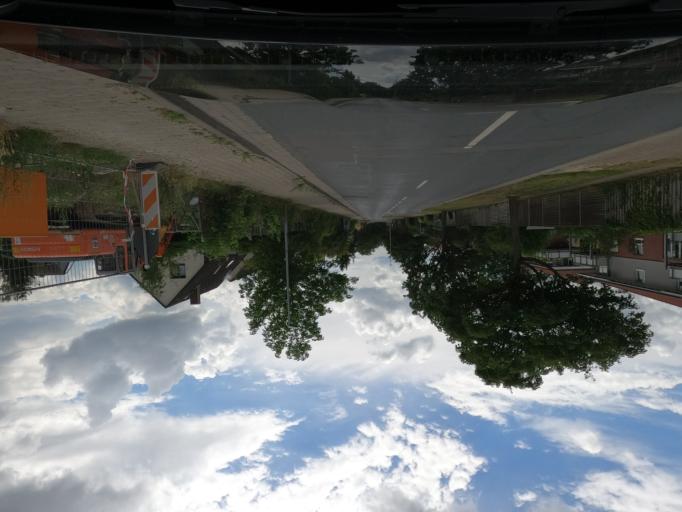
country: DE
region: Lower Saxony
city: Sehnde
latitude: 52.3498
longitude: 9.8985
